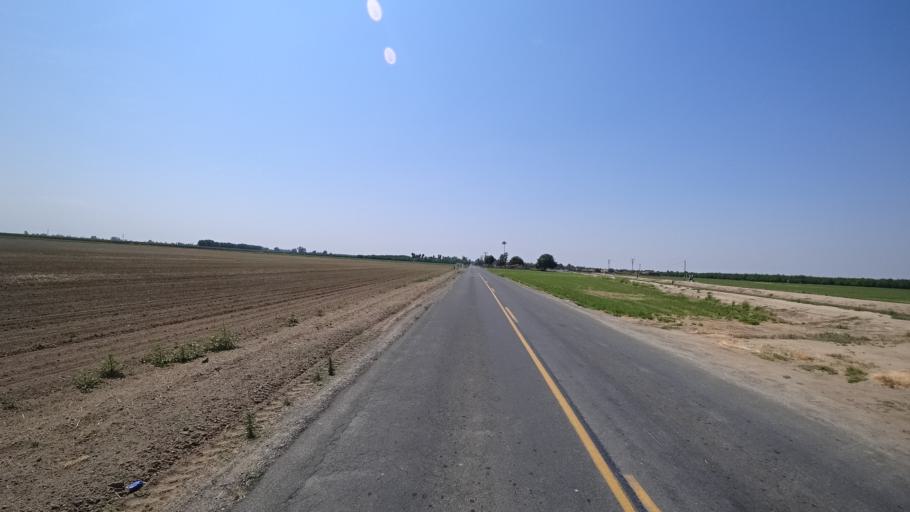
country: US
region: California
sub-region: Kings County
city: Lemoore
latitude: 36.3275
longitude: -119.7628
